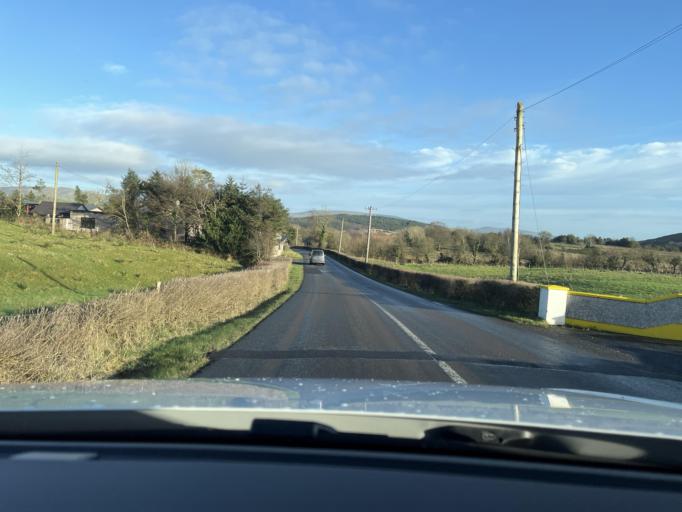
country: IE
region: Connaught
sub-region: County Leitrim
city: Manorhamilton
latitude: 54.3030
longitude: -8.2406
